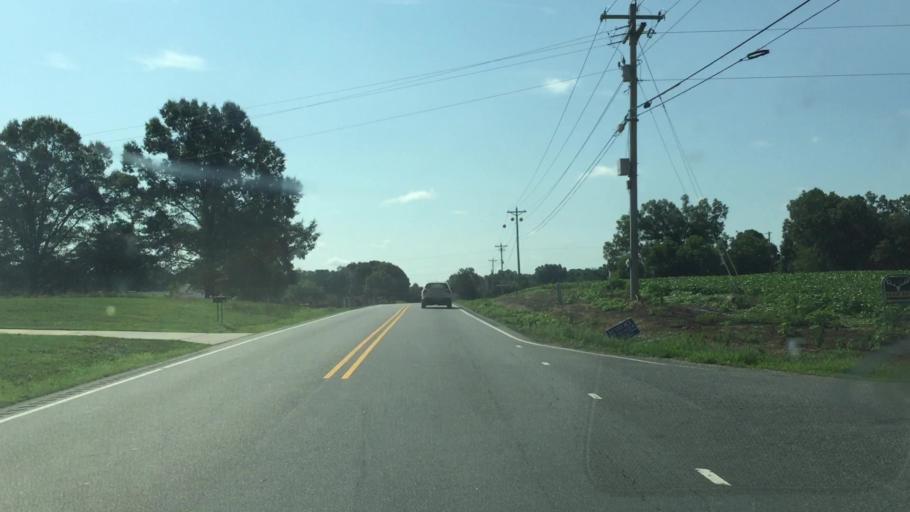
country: US
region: North Carolina
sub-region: Union County
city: Fairview
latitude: 35.1577
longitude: -80.5648
